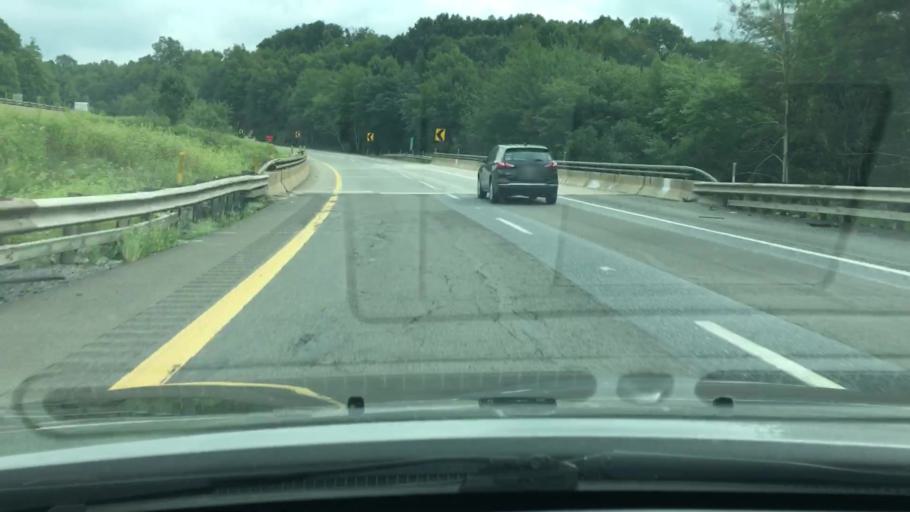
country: US
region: Pennsylvania
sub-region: Schuylkill County
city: Tremont
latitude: 40.6275
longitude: -76.4485
